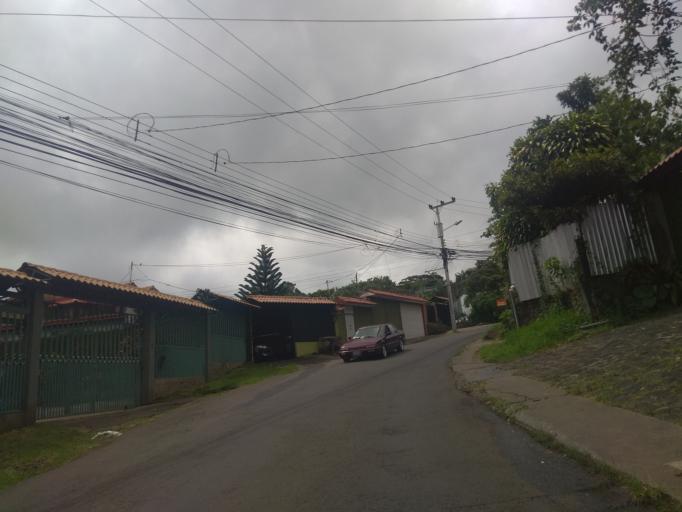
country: CR
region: Heredia
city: San Josecito
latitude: 10.0304
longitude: -84.1079
